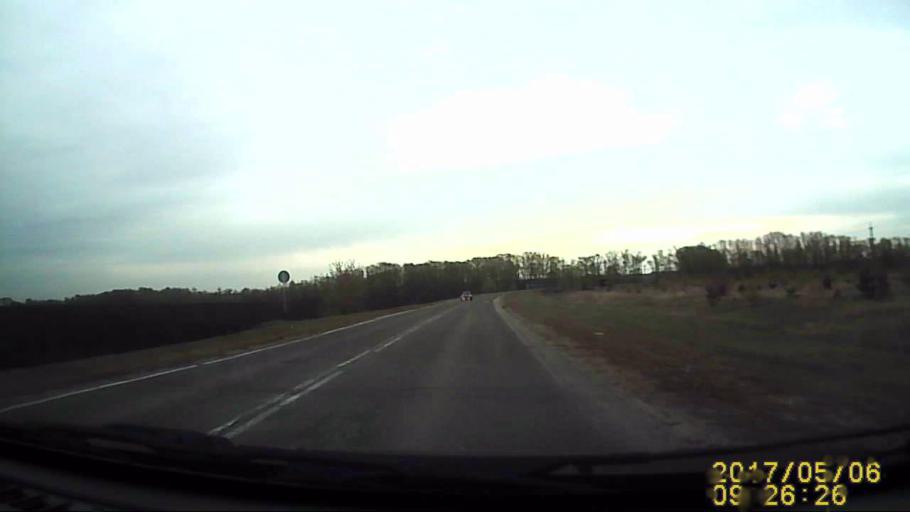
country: RU
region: Ulyanovsk
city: Cherdakly
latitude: 54.3849
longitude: 48.8358
